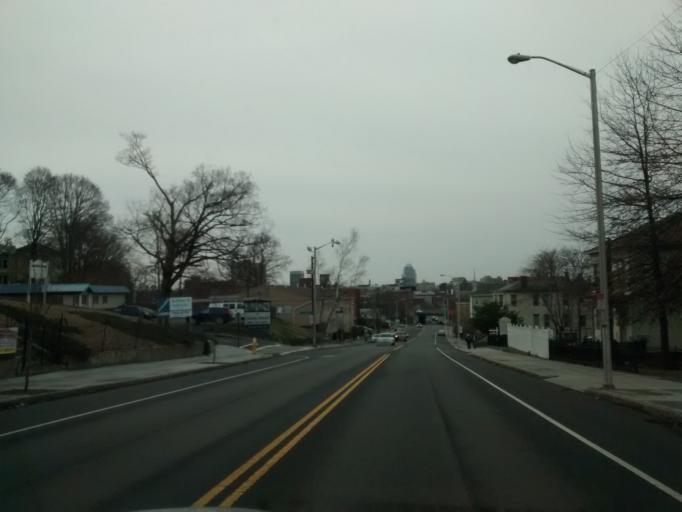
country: US
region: Massachusetts
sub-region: Worcester County
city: Worcester
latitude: 42.2782
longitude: -71.7943
